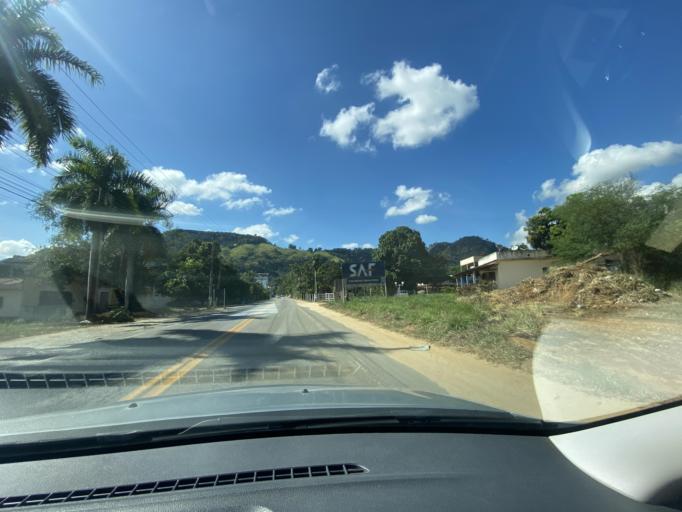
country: BR
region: Espirito Santo
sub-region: Jeronimo Monteiro
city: Jeronimo Monteiro
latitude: -20.7943
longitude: -41.4065
